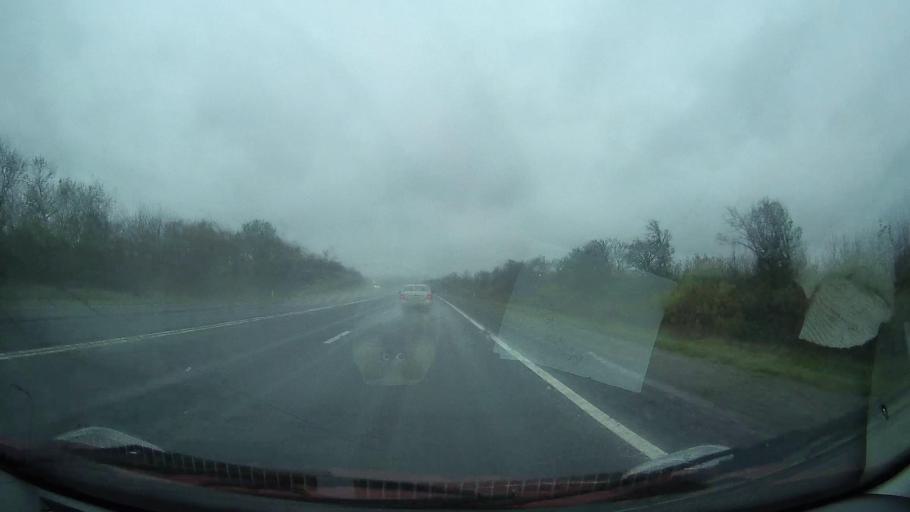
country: RU
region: Stavropol'skiy
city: Nevinnomyssk
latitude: 44.6194
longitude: 42.0942
